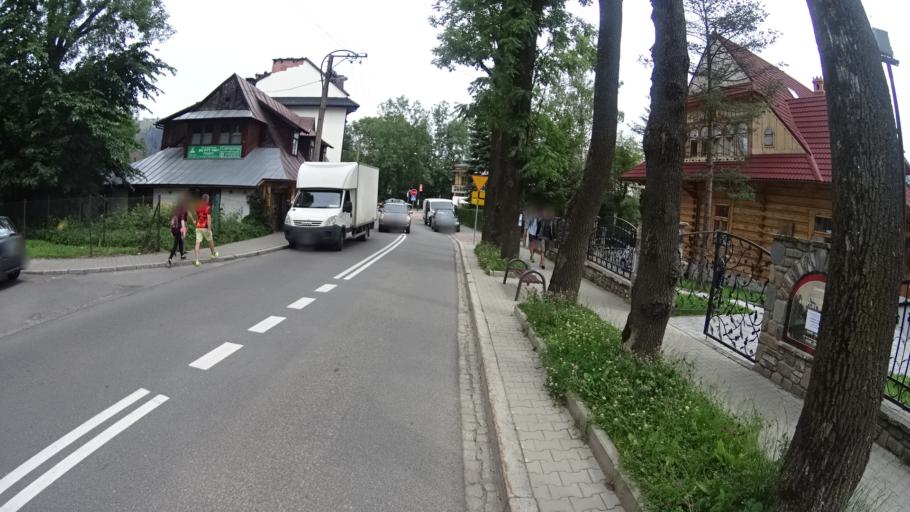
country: PL
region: Lesser Poland Voivodeship
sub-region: Powiat tatrzanski
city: Zakopane
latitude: 49.2910
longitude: 19.9481
